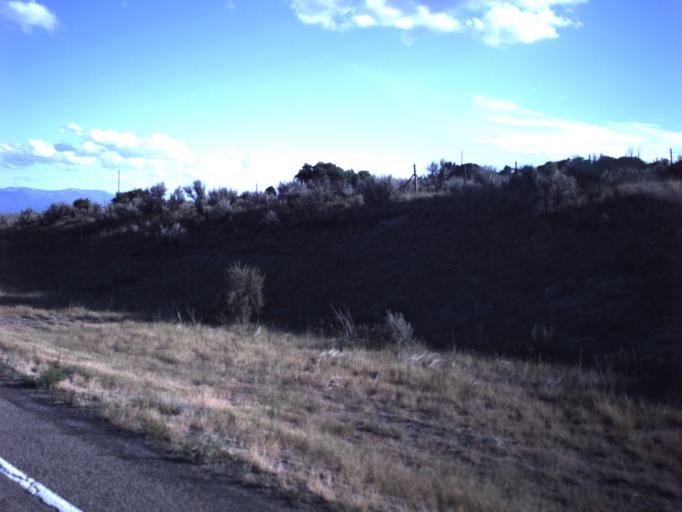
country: US
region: Utah
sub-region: Sanpete County
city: Fairview
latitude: 39.6952
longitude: -111.4624
